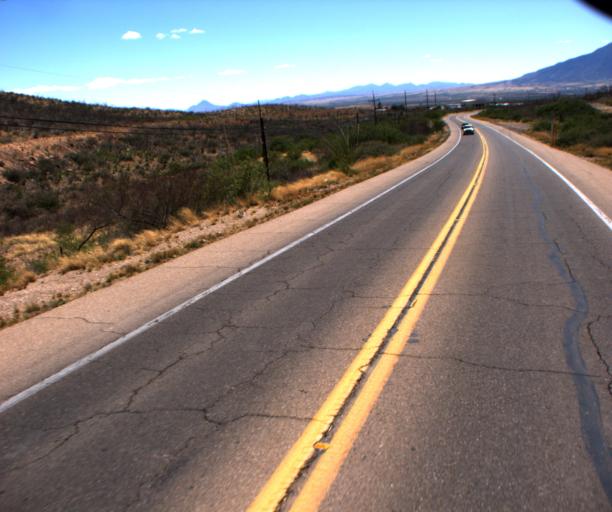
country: US
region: Arizona
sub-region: Cochise County
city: Bisbee
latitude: 31.4127
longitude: -109.9004
